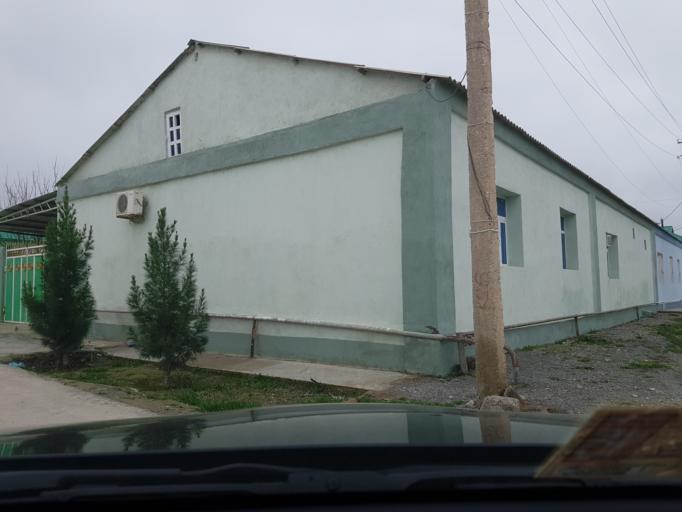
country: TM
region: Ahal
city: Abadan
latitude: 38.1418
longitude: 57.9475
